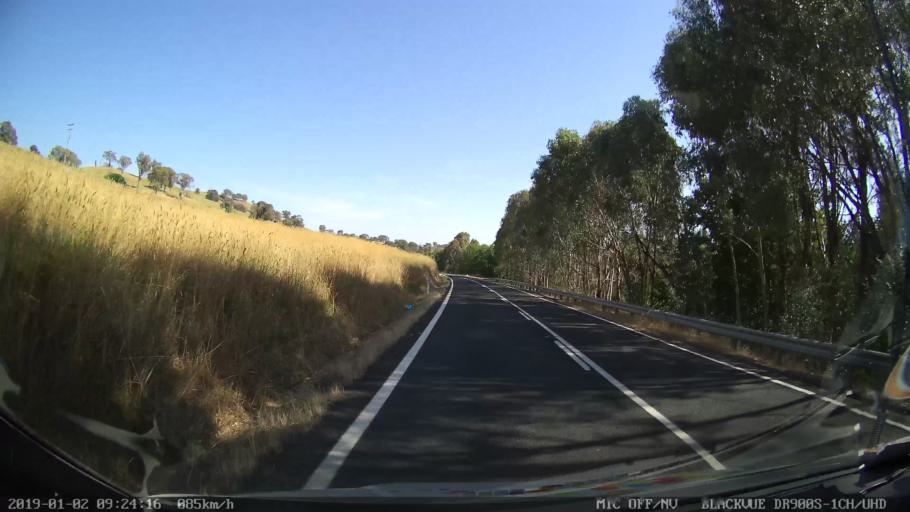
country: AU
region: New South Wales
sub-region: Tumut Shire
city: Tumut
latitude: -35.3793
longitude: 148.2921
